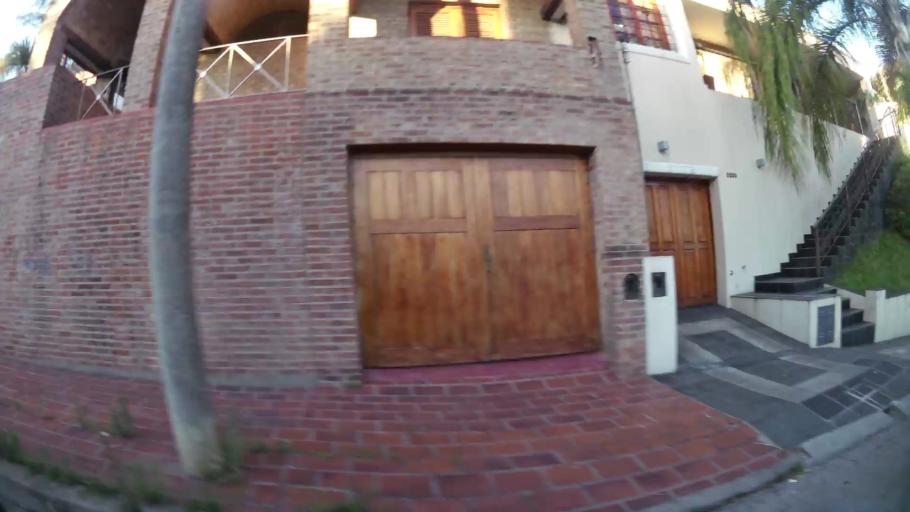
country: AR
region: Cordoba
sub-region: Departamento de Capital
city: Cordoba
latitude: -31.3837
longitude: -64.2100
